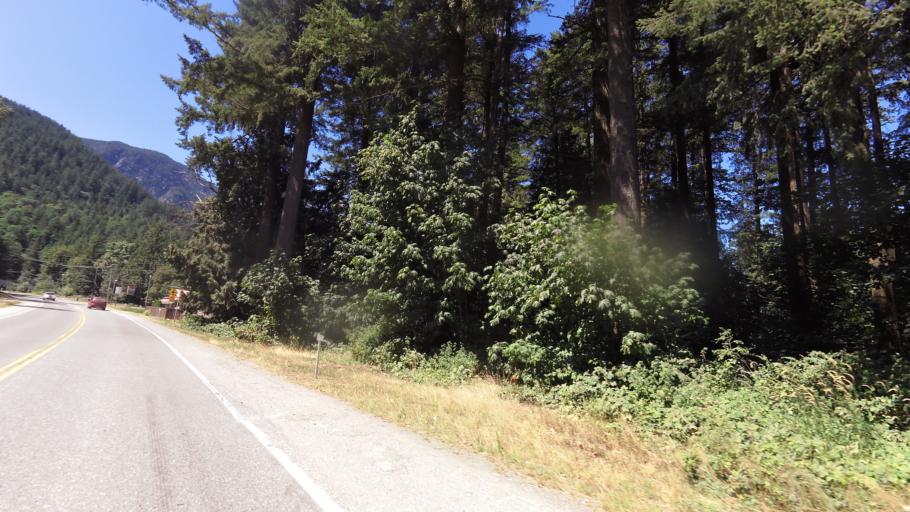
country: CA
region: British Columbia
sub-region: Fraser Valley Regional District
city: Chilliwack
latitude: 49.2505
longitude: -121.9510
